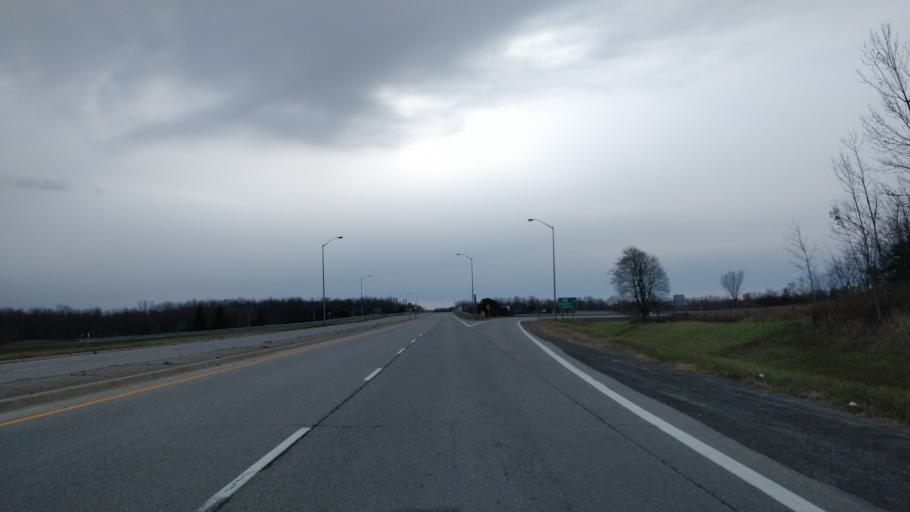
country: CA
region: Ontario
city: Prescott
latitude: 44.7570
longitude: -75.4809
